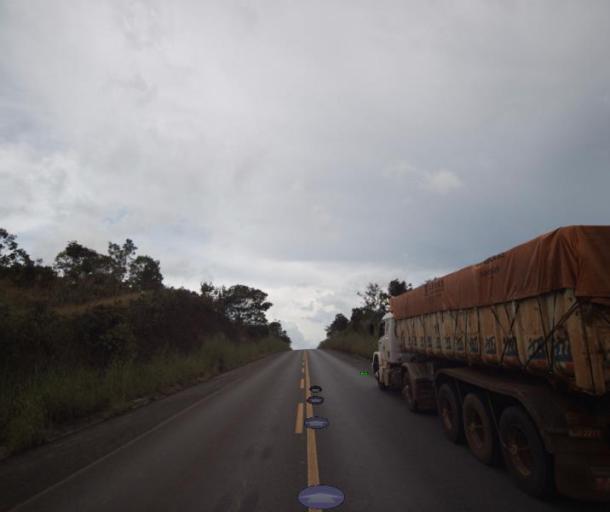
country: BR
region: Goias
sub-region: Niquelandia
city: Niquelandia
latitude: -14.4996
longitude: -48.4997
